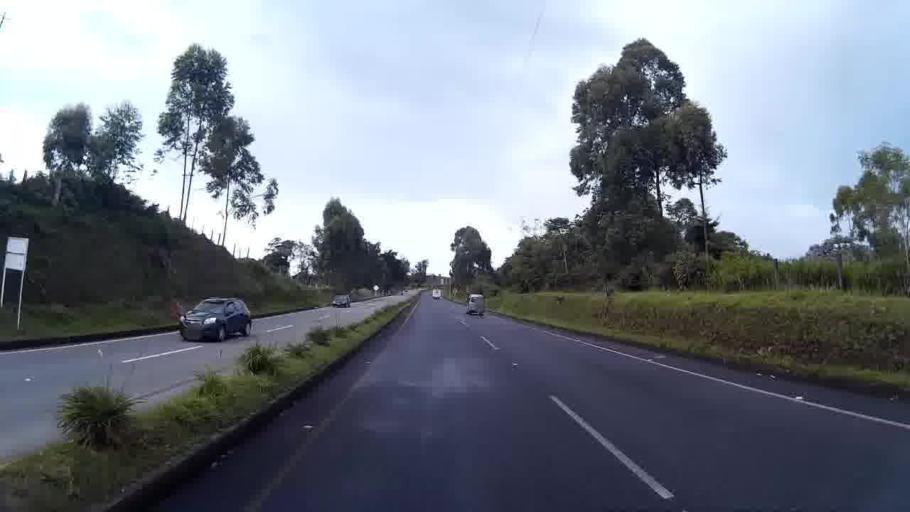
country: CO
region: Quindio
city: Circasia
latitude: 4.6398
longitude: -75.6103
